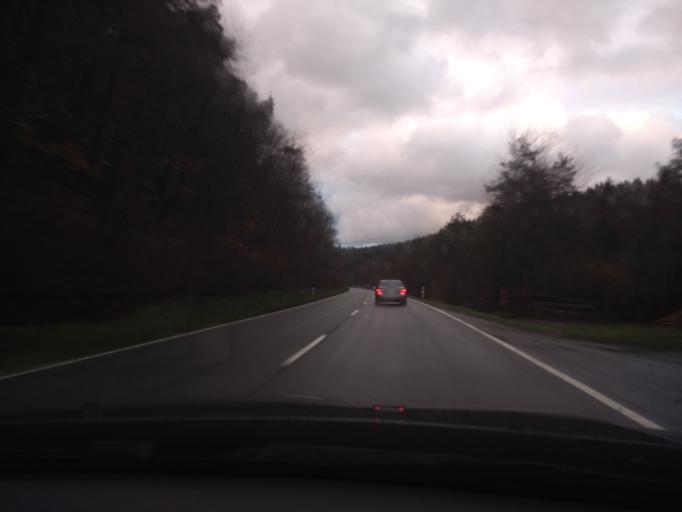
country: DE
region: Rheinland-Pfalz
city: Breit
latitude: 49.7697
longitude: 6.8979
